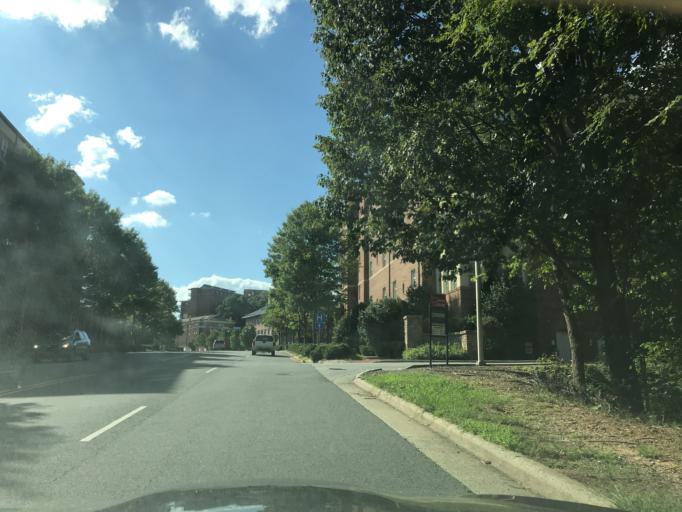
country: US
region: North Carolina
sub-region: Orange County
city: Chapel Hill
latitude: 35.9031
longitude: -79.0429
